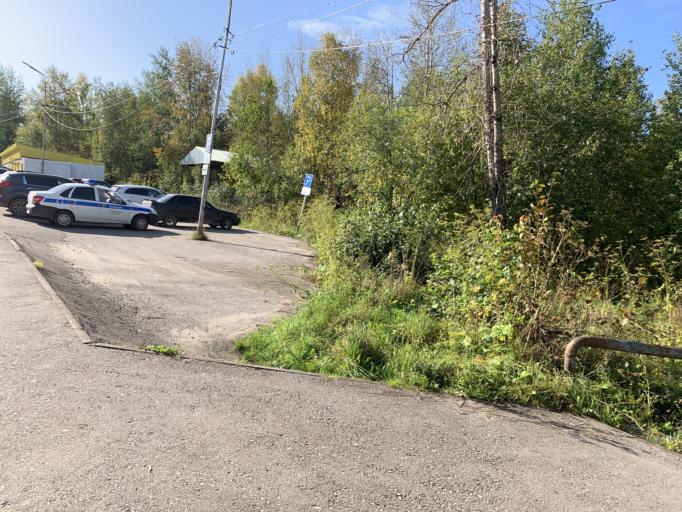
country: RU
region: Perm
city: Gubakha
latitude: 58.8425
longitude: 57.5536
